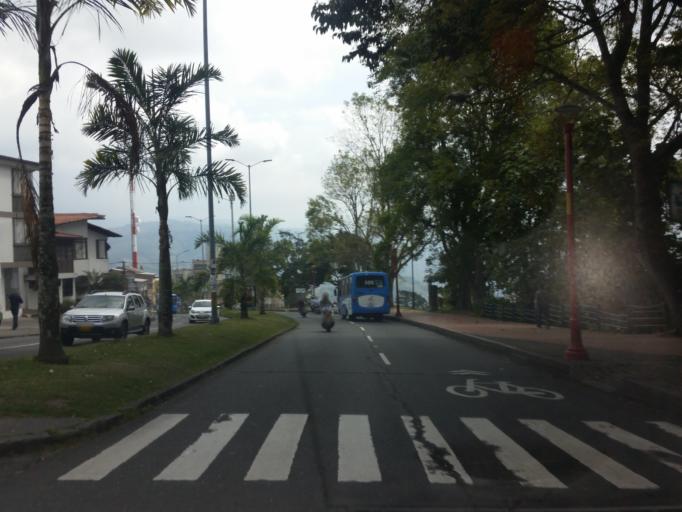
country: CO
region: Caldas
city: Manizales
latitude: 5.0707
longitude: -75.5246
